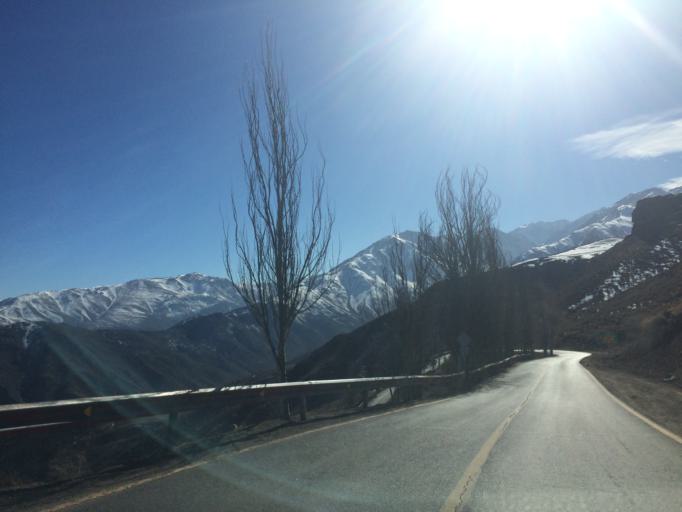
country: CL
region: Santiago Metropolitan
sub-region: Provincia de Santiago
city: Villa Presidente Frei, Nunoa, Santiago, Chile
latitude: -33.3567
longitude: -70.3199
